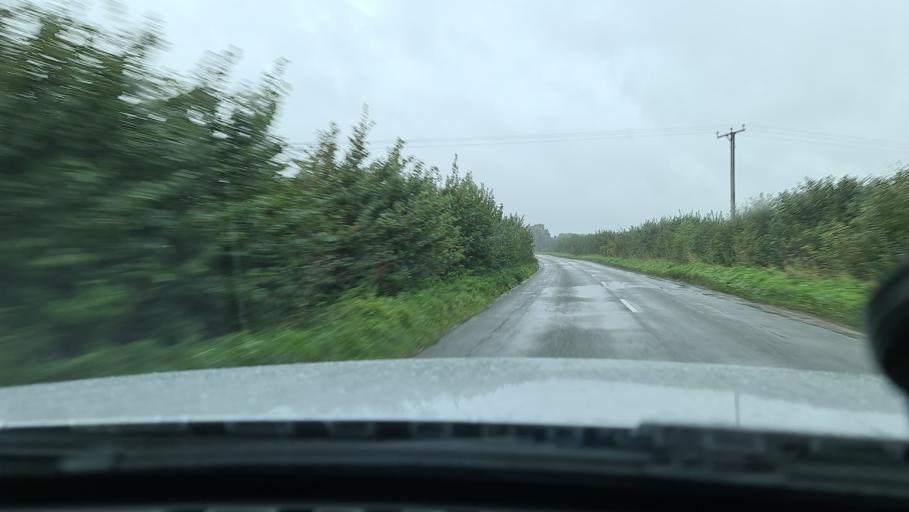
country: GB
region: England
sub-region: Oxfordshire
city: Somerton
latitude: 51.9259
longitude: -1.2775
